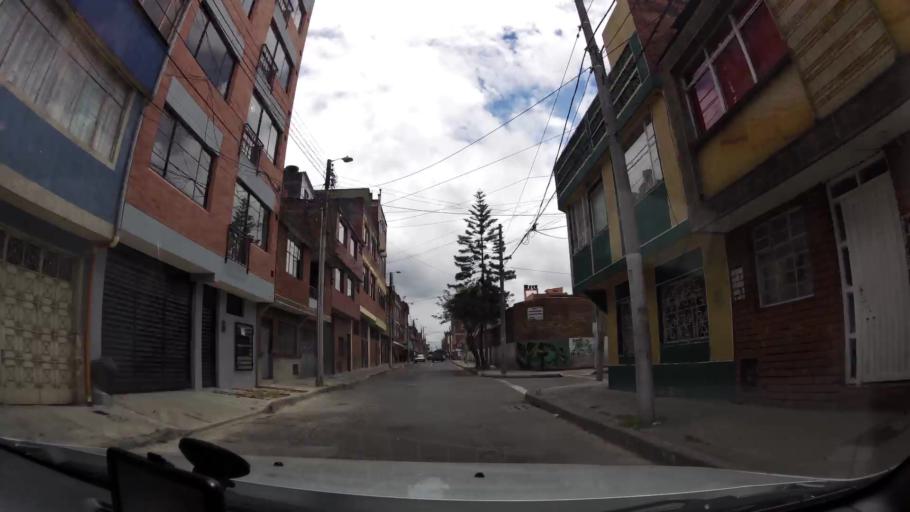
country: CO
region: Bogota D.C.
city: Bogota
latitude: 4.6026
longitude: -74.1073
